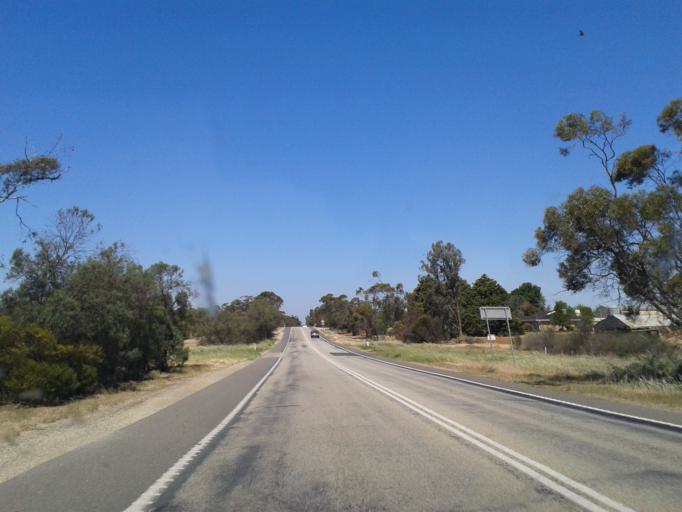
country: AU
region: Victoria
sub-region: Swan Hill
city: Swan Hill
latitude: -35.1923
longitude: 143.3800
